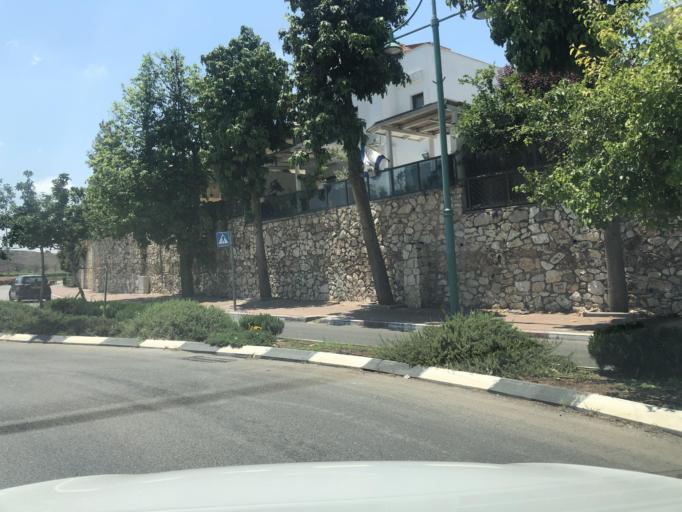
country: IL
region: Haifa
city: Daliyat el Karmil
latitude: 32.6373
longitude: 35.0847
